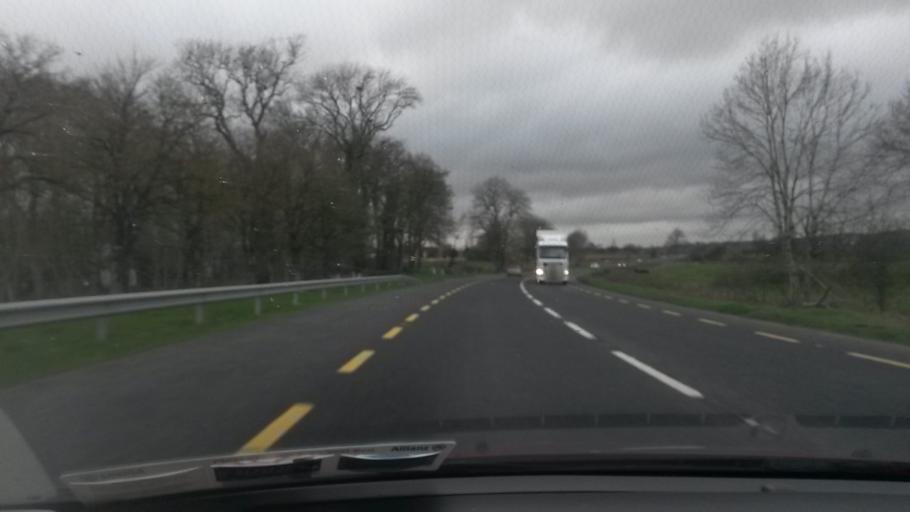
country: IE
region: Munster
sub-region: County Limerick
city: Abbeyfeale
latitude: 52.3823
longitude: -9.2236
